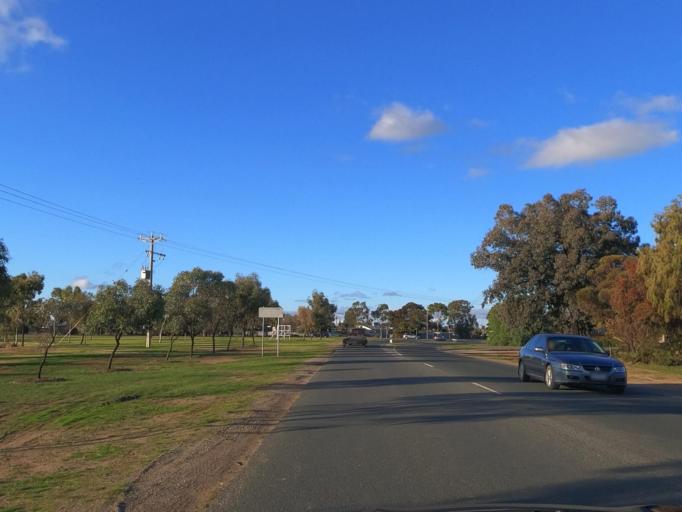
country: AU
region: Victoria
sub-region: Swan Hill
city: Swan Hill
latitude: -35.3402
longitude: 143.5387
